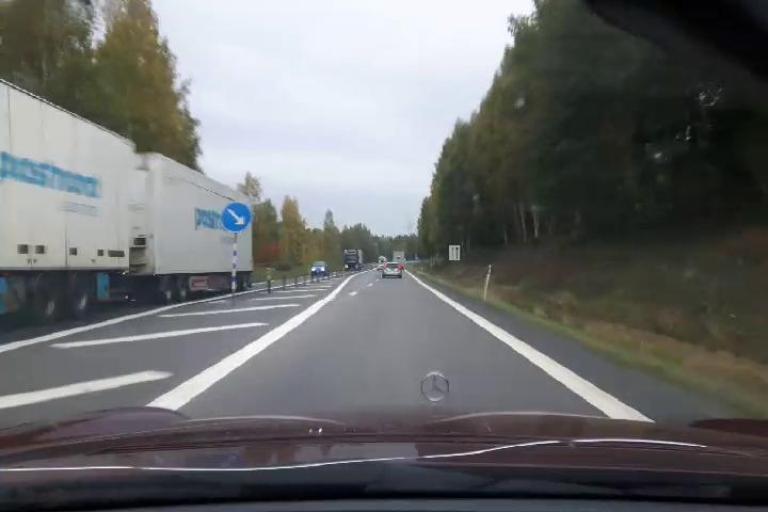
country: SE
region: Vaesternorrland
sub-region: Kramfors Kommun
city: Nordingra
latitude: 63.0625
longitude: 18.3542
